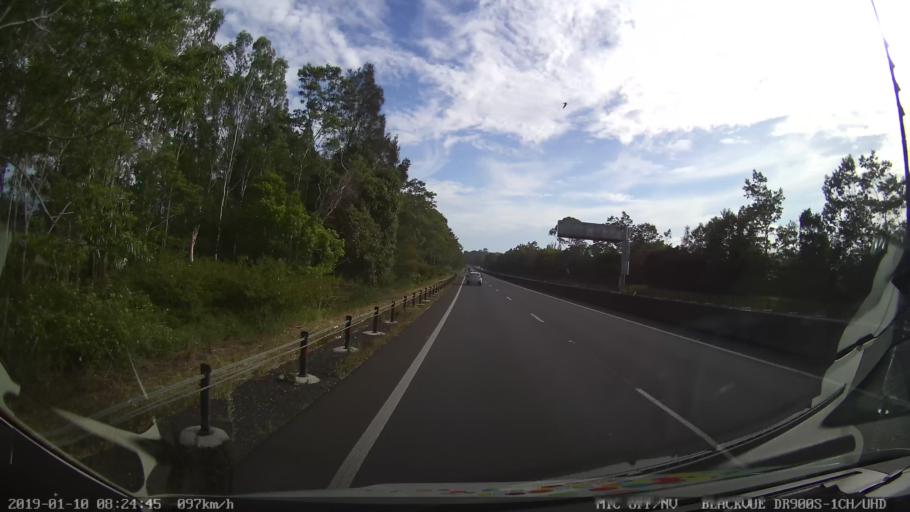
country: AU
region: New South Wales
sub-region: Coffs Harbour
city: Bonville
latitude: -30.4426
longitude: 153.0108
